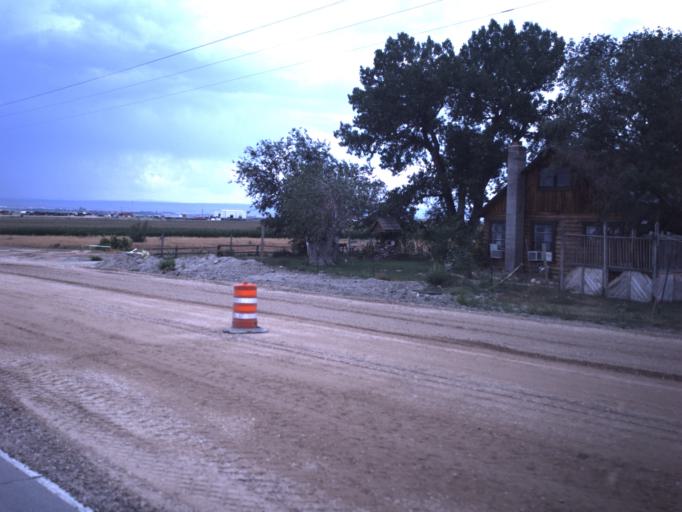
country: US
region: Utah
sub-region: Duchesne County
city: Roosevelt
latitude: 40.2254
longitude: -110.0674
